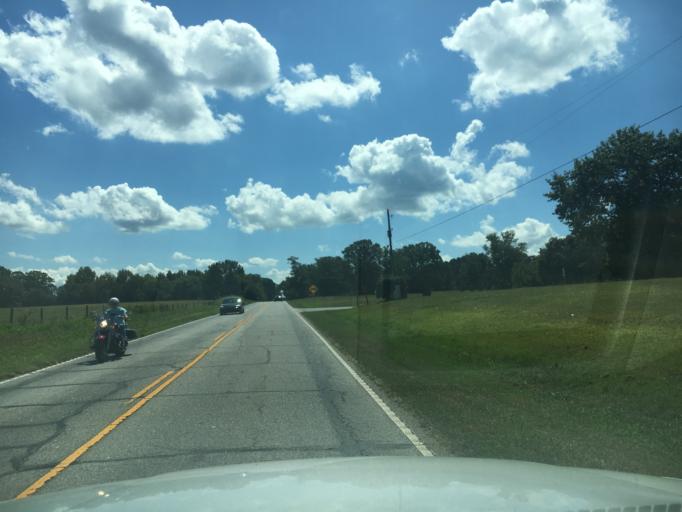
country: US
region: South Carolina
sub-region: Laurens County
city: Laurens
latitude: 34.5125
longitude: -82.0899
